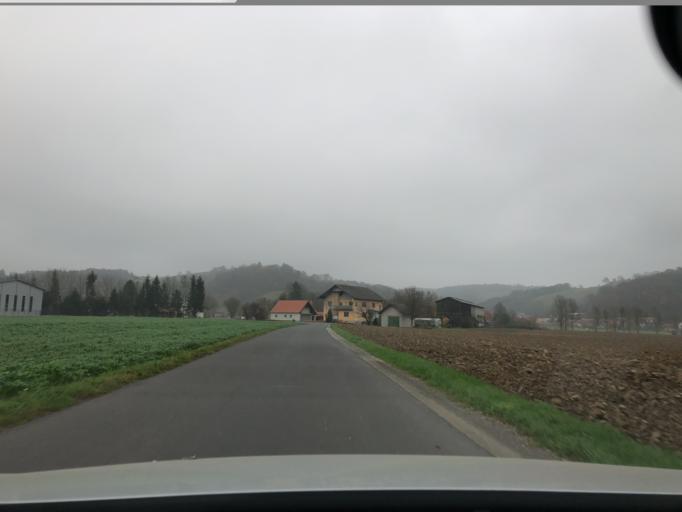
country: AT
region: Styria
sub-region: Politischer Bezirk Suedoststeiermark
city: Fehring
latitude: 46.9500
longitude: 16.0341
